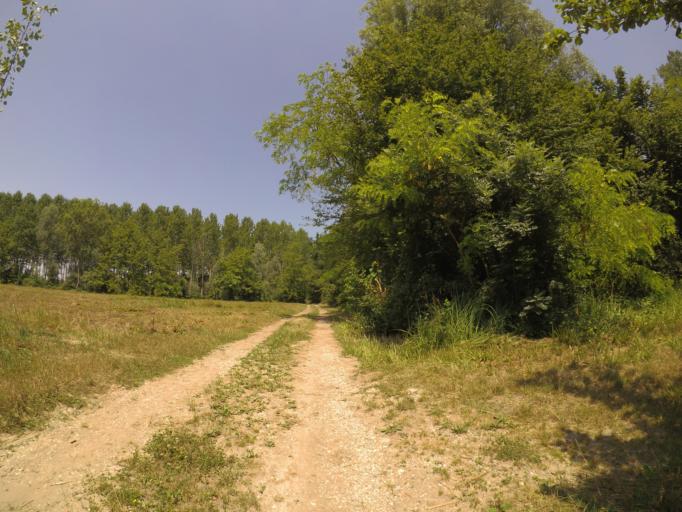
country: IT
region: Friuli Venezia Giulia
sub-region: Provincia di Udine
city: Rivignano
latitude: 45.8974
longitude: 13.0396
